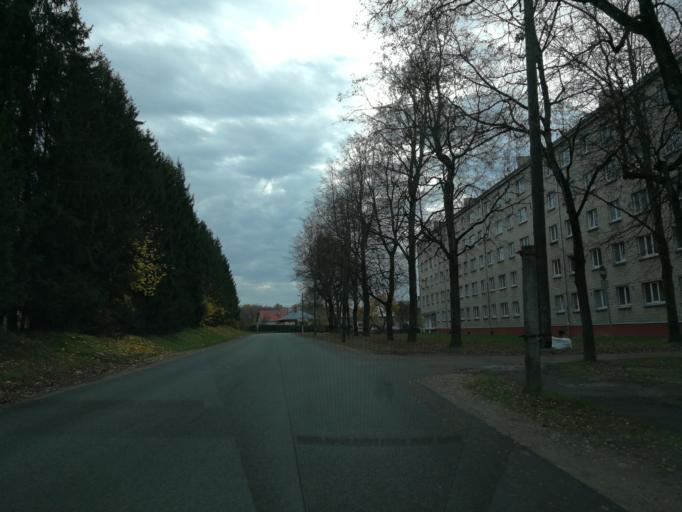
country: LV
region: Cesu Rajons
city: Cesis
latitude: 57.3061
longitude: 25.2751
